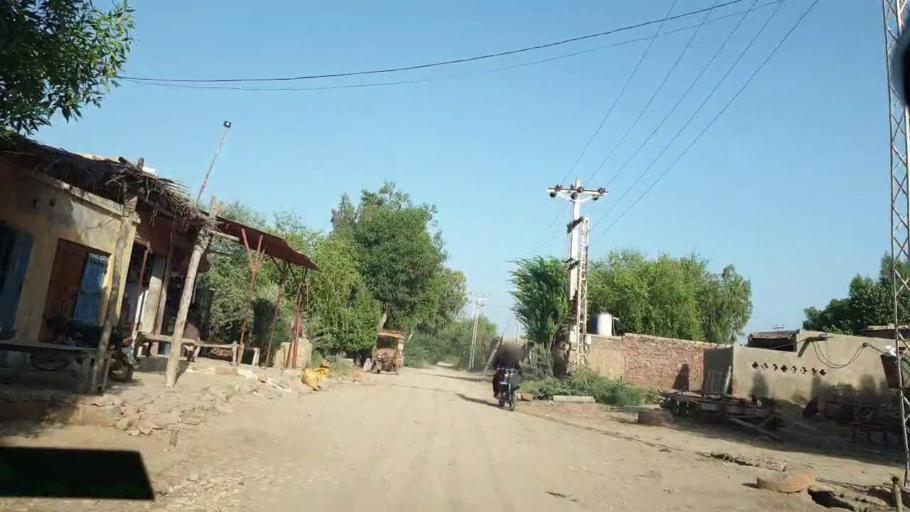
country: PK
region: Sindh
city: Naukot
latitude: 24.7407
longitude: 69.2269
